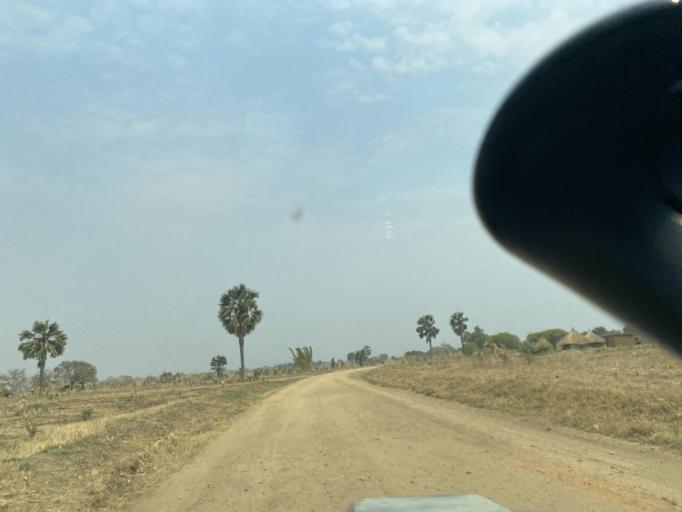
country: ZM
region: Lusaka
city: Kafue
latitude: -15.6513
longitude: 28.0505
